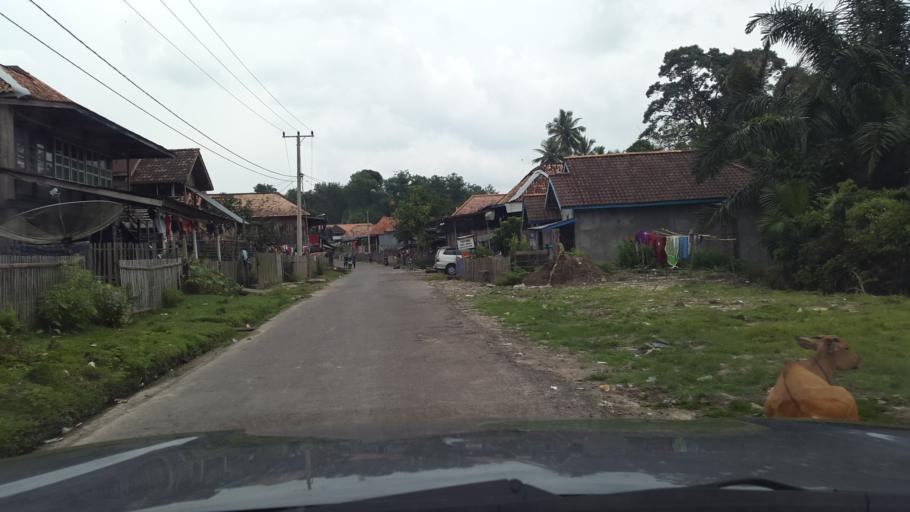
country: ID
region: South Sumatra
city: Gunungmenang
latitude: -3.1159
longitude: 103.8424
